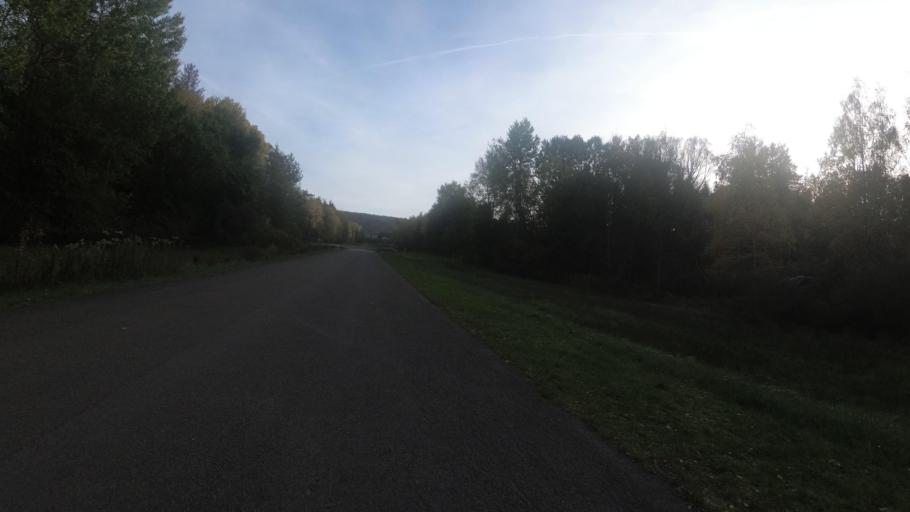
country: DE
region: Rheinland-Pfalz
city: Steinwenden
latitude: 49.4229
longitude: 7.5308
